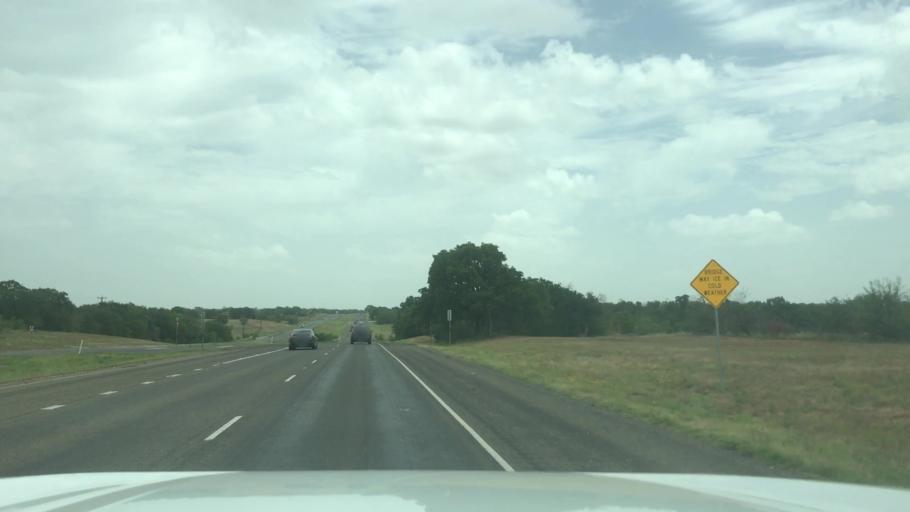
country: US
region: Texas
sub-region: McLennan County
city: Riesel
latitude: 31.5045
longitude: -96.9444
